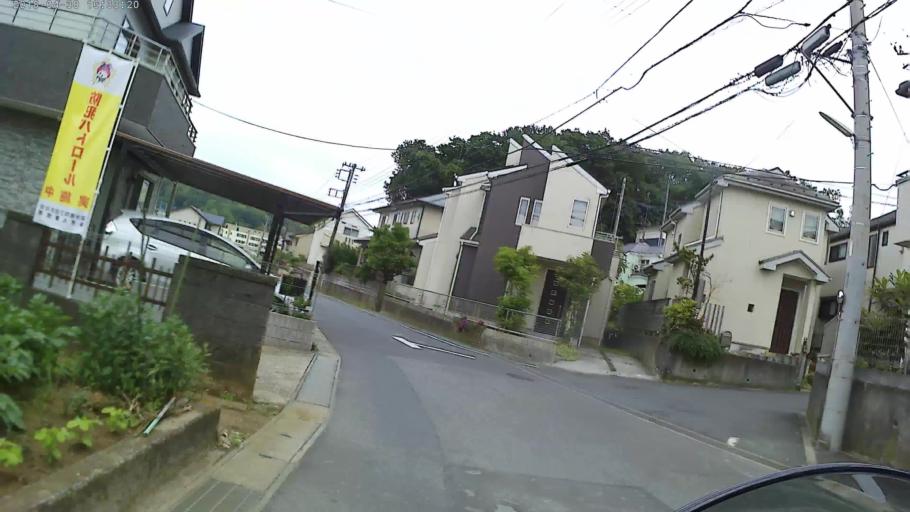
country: JP
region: Kanagawa
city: Zama
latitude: 35.4501
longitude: 139.4035
